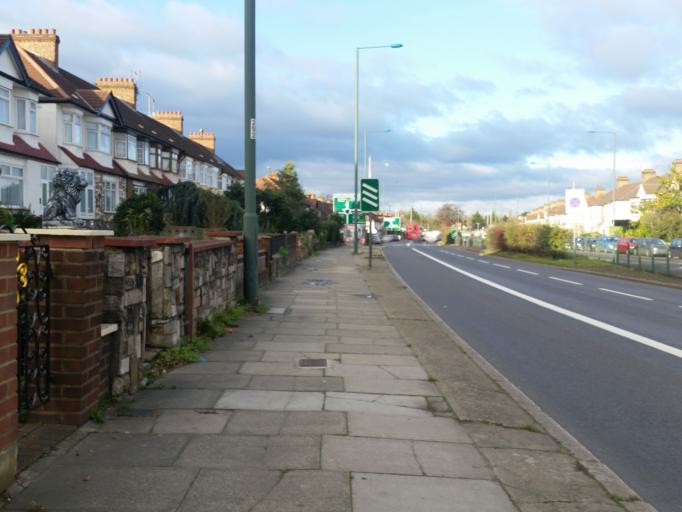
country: GB
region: England
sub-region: Greater London
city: Wood Green
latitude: 51.6131
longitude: -0.0869
